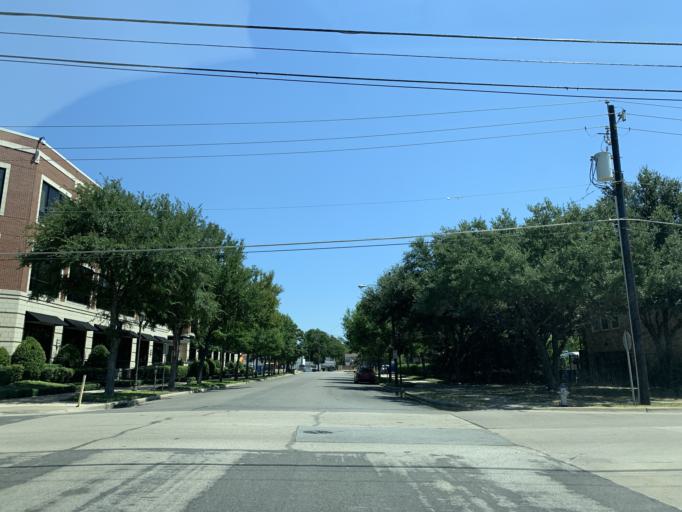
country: US
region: Texas
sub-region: Dallas County
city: Dallas
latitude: 32.7902
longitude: -96.7749
